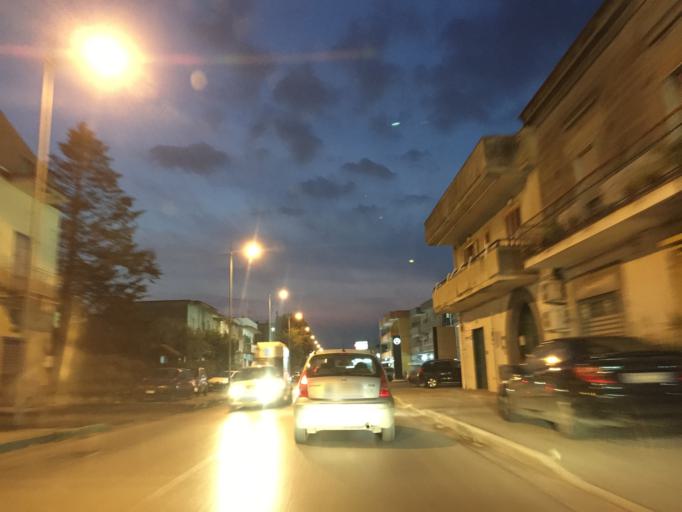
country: IT
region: Campania
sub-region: Provincia di Salerno
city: San Lorenzo
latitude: 40.7480
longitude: 14.5913
